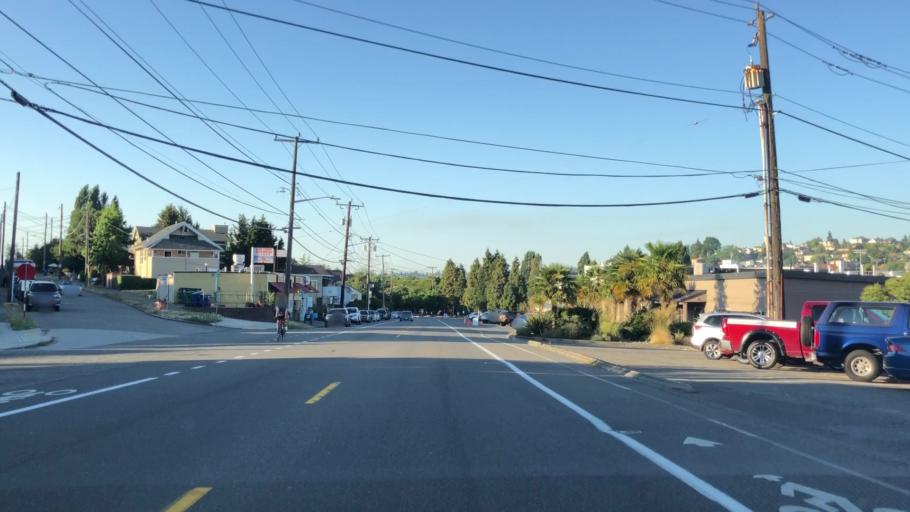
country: US
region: Washington
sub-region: King County
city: Seattle
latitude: 47.6445
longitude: -122.3834
